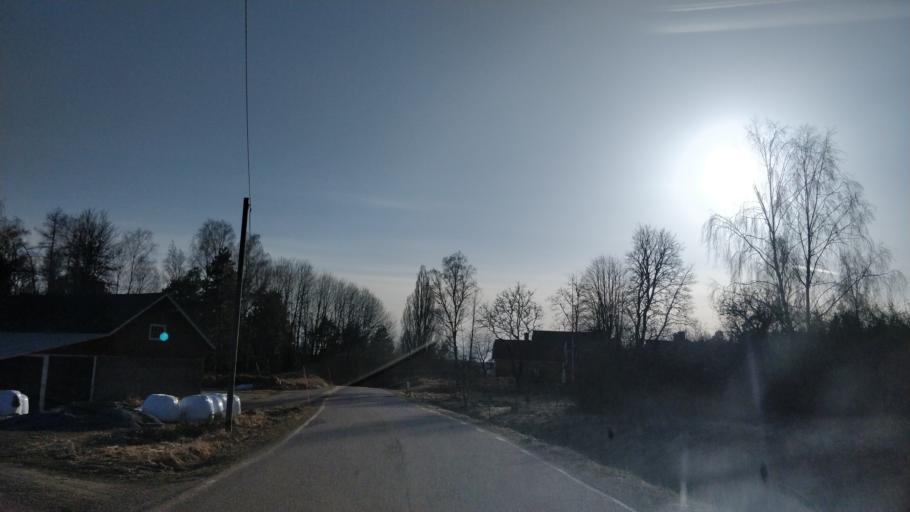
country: SE
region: Uppsala
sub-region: Enkopings Kommun
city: Orsundsbro
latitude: 59.7485
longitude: 17.2224
